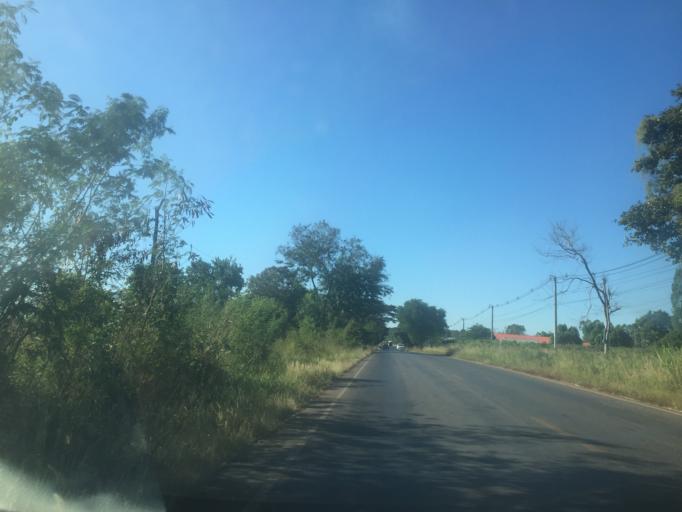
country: TH
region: Kalasin
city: Tha Khantho
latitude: 16.9651
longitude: 103.2463
